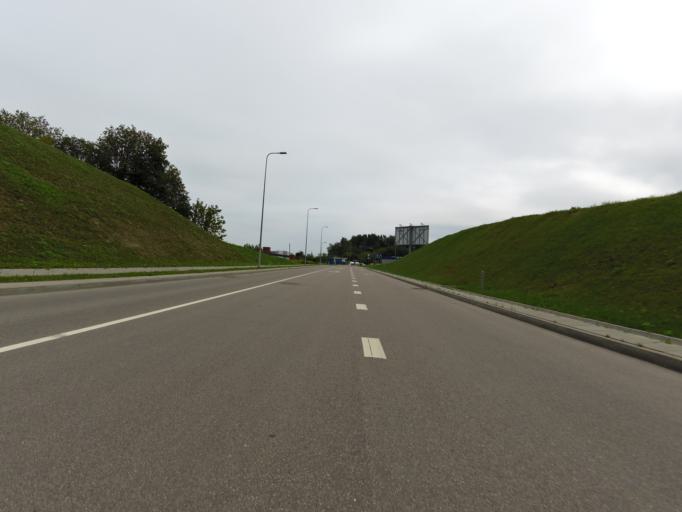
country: LT
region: Vilnius County
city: Naujamiestis
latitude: 54.6566
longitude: 25.2897
